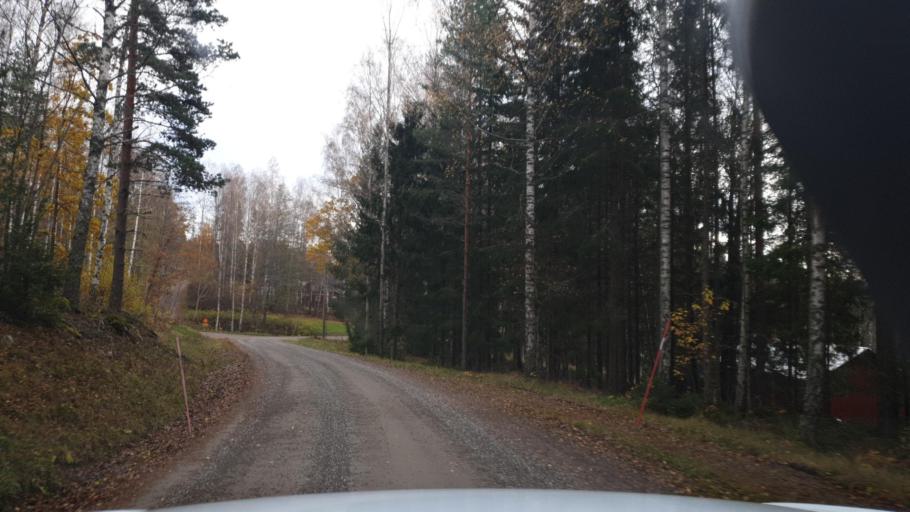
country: SE
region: Vaermland
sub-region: Arvika Kommun
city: Arvika
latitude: 59.5088
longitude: 12.7293
